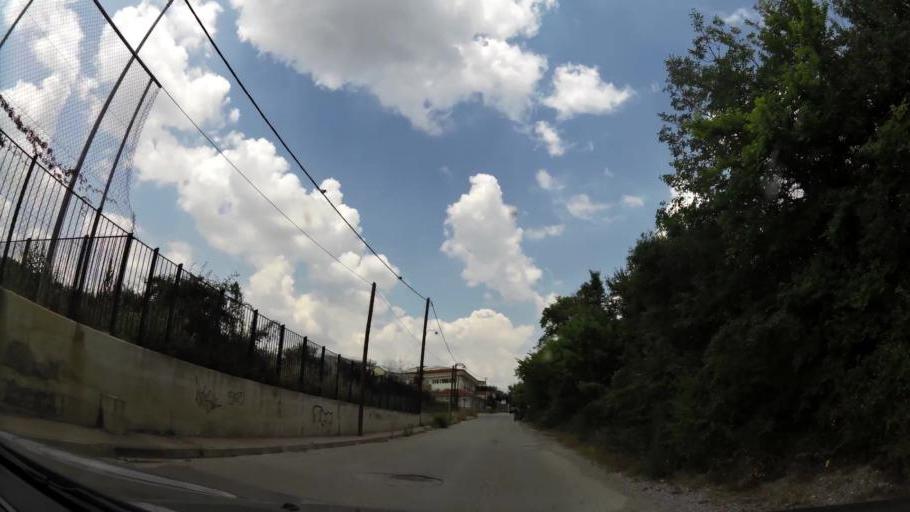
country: GR
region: West Macedonia
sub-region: Nomos Kozanis
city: Kozani
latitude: 40.3016
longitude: 21.8053
